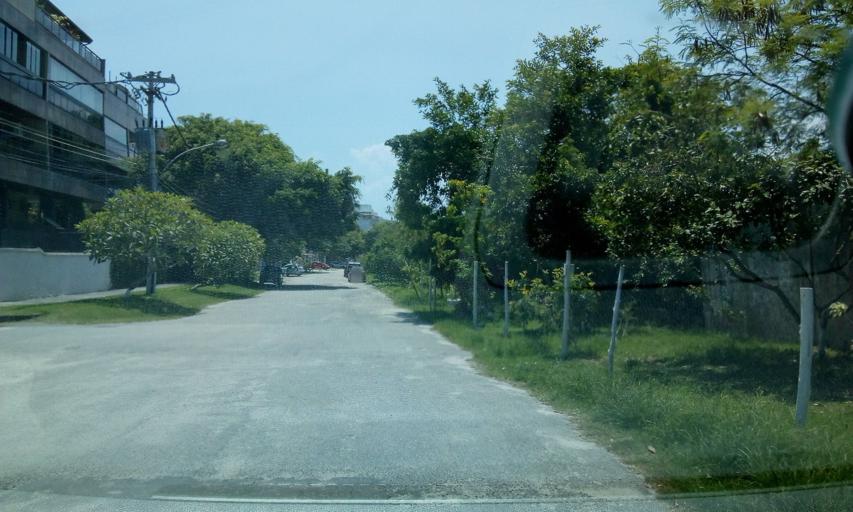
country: BR
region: Rio de Janeiro
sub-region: Nilopolis
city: Nilopolis
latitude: -23.0277
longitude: -43.4697
